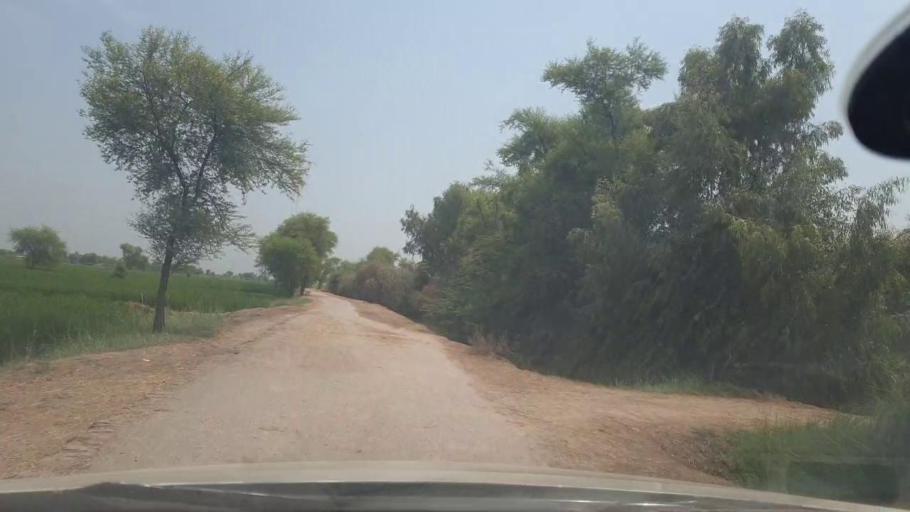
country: PK
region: Sindh
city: Jacobabad
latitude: 28.1777
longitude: 68.3827
